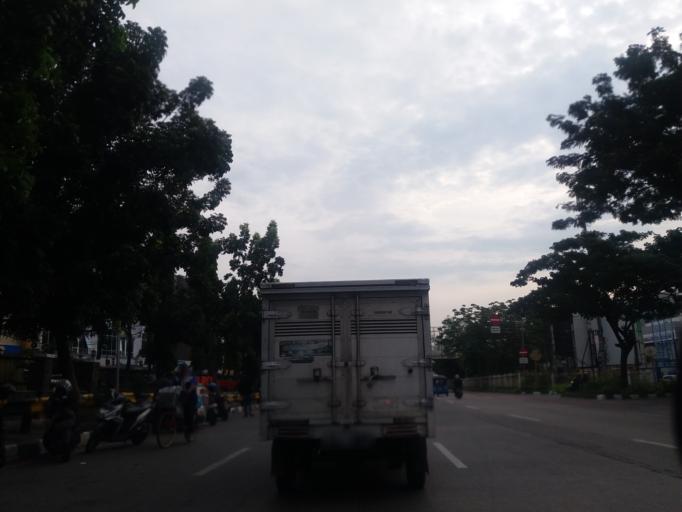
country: ID
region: Jakarta Raya
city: Jakarta
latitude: -6.1354
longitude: 106.8305
